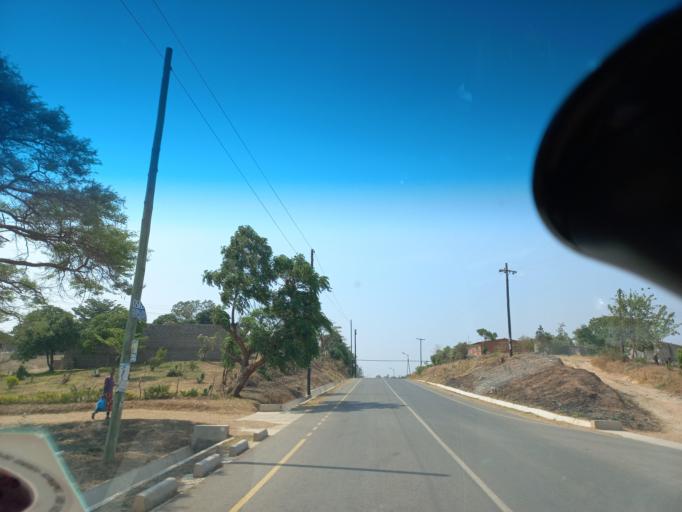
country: ZM
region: Lusaka
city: Lusaka
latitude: -15.5662
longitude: 28.2689
